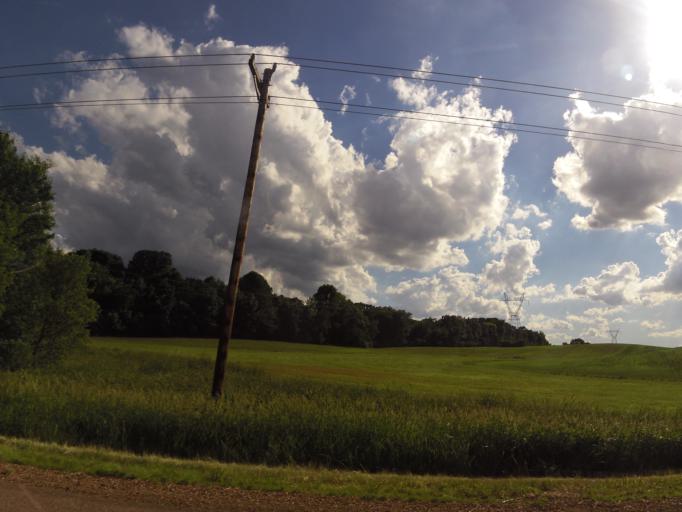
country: US
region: Minnesota
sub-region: Carver County
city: Victoria
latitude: 44.8137
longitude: -93.6829
